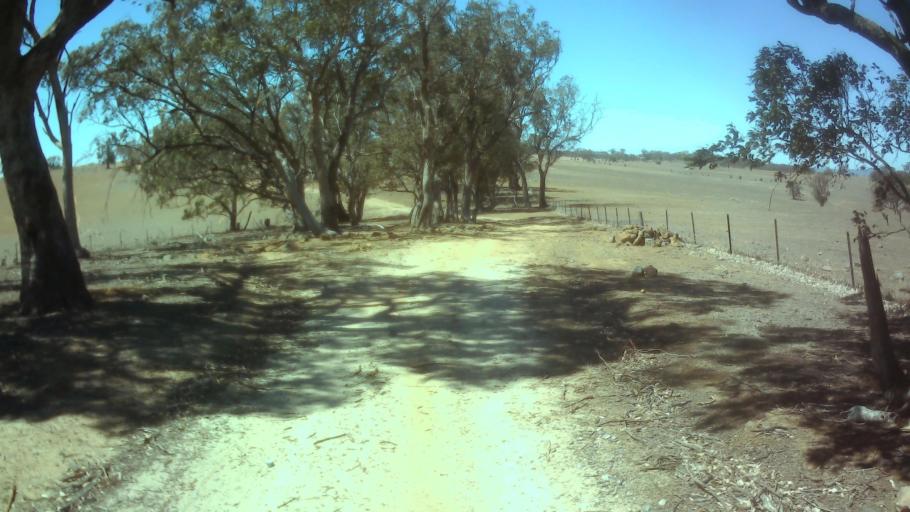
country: AU
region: New South Wales
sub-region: Cowra
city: Cowra
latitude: -33.8974
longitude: 148.5063
